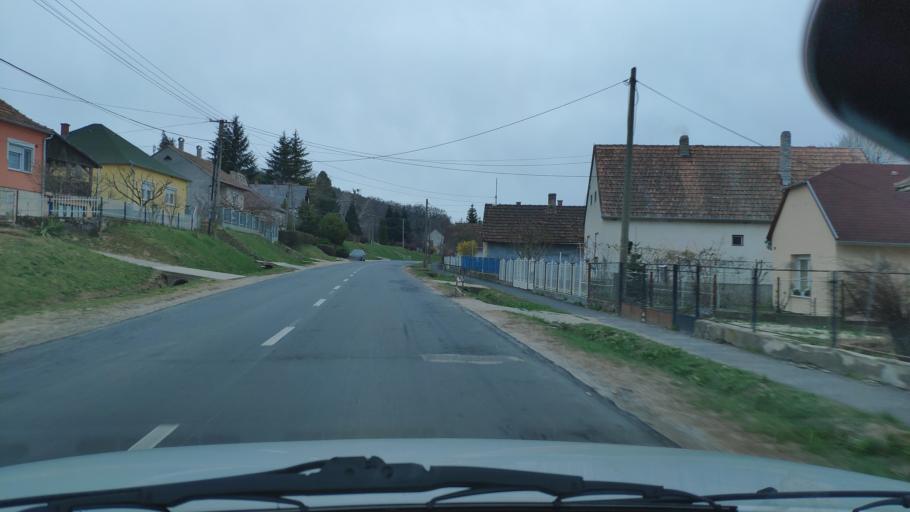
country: HU
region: Zala
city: Nagykanizsa
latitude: 46.5398
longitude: 16.9855
